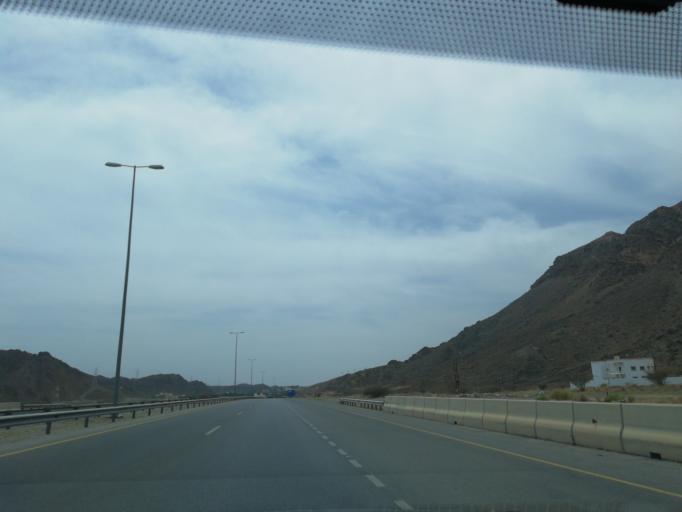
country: OM
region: Muhafazat ad Dakhiliyah
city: Izki
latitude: 23.1316
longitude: 57.8408
